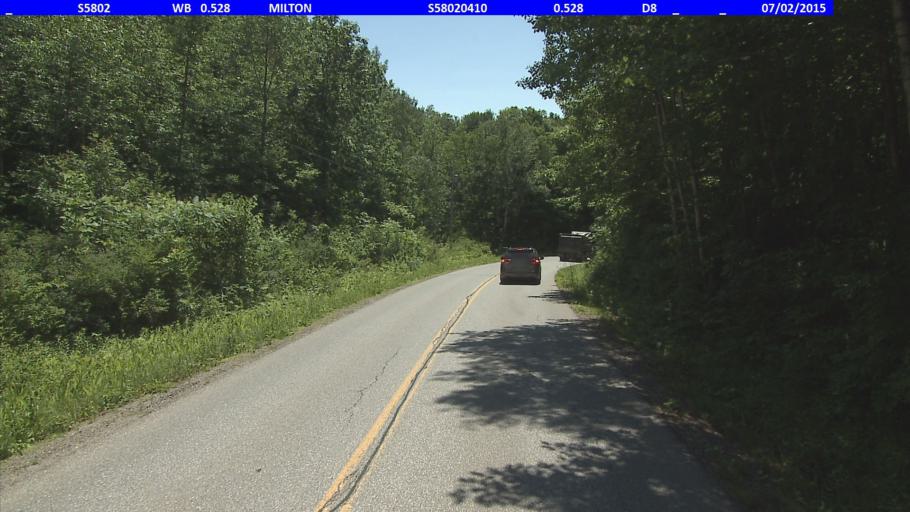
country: US
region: Vermont
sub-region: Chittenden County
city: Colchester
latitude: 44.6155
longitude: -73.2032
